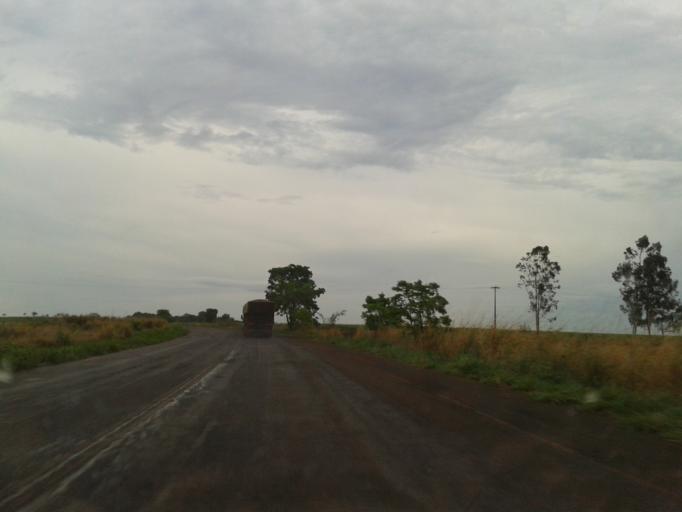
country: BR
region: Goias
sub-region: Santa Helena De Goias
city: Santa Helena de Goias
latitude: -18.0539
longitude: -50.4822
